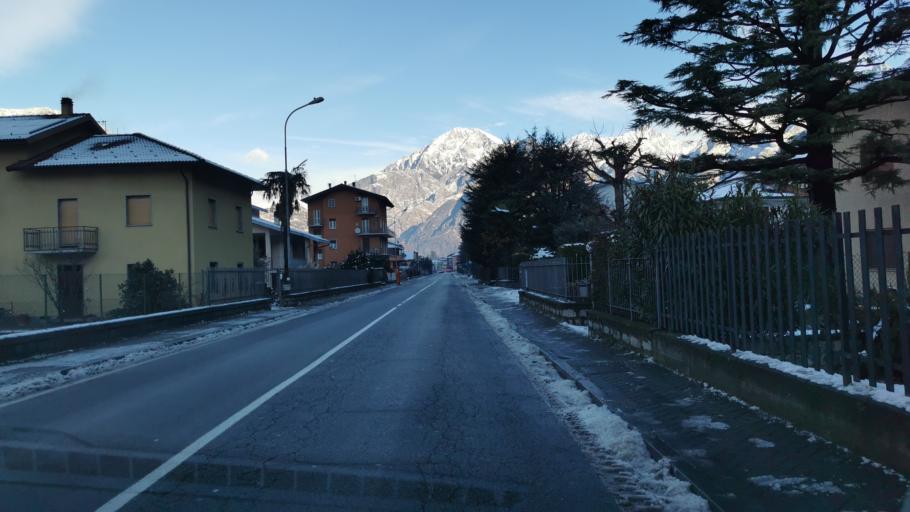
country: IT
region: Lombardy
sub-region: Provincia di Sondrio
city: Dubino
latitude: 46.1672
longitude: 9.4320
